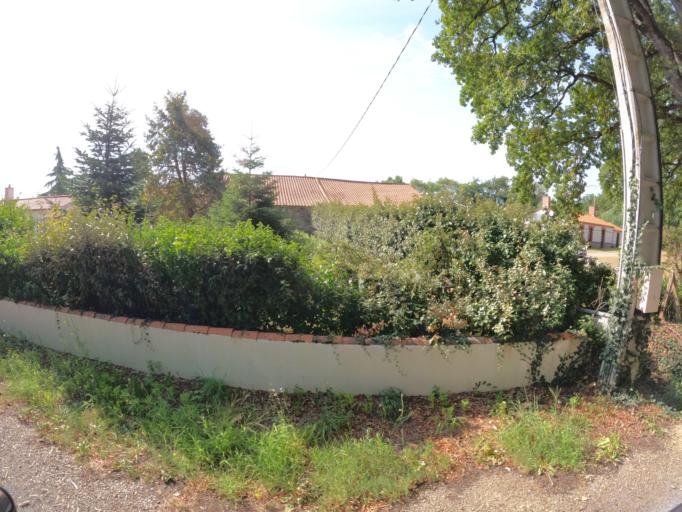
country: FR
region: Pays de la Loire
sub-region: Departement de la Vendee
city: Challans
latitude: 46.8074
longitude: -1.8647
